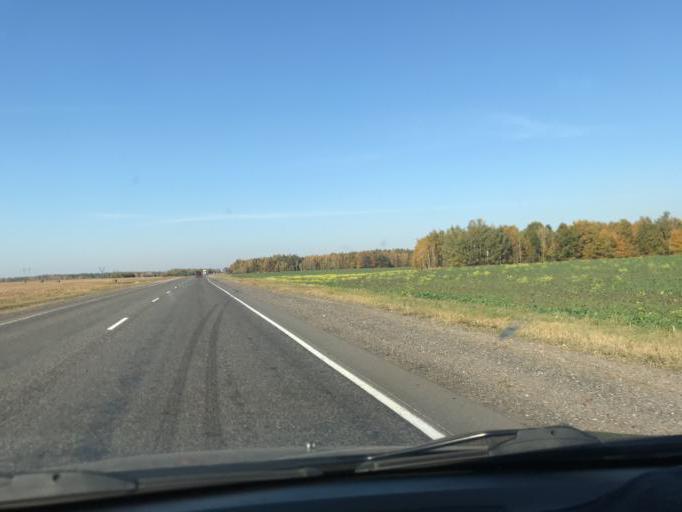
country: BY
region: Mogilev
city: Babruysk
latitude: 53.0939
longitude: 29.0602
